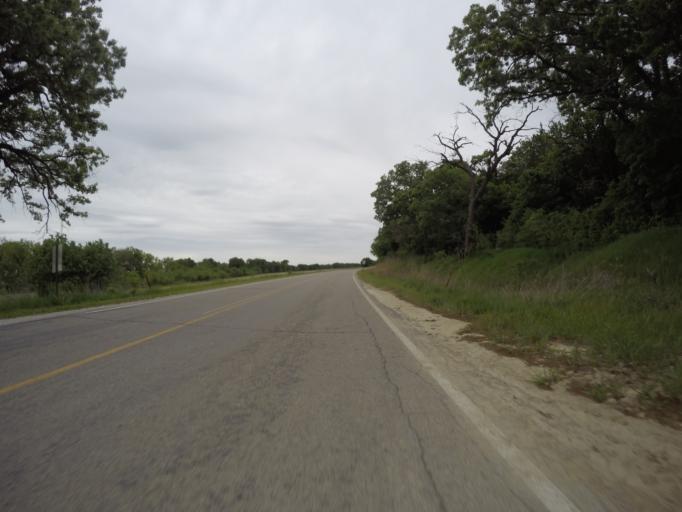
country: US
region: Kansas
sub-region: Pottawatomie County
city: Wamego
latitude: 39.1863
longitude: -96.3336
